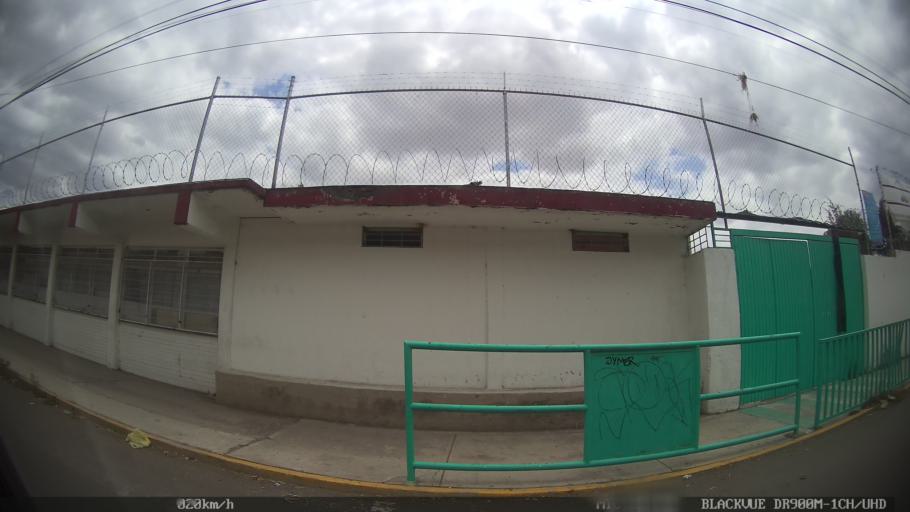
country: MX
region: Jalisco
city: Tonala
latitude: 20.6361
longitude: -103.2605
